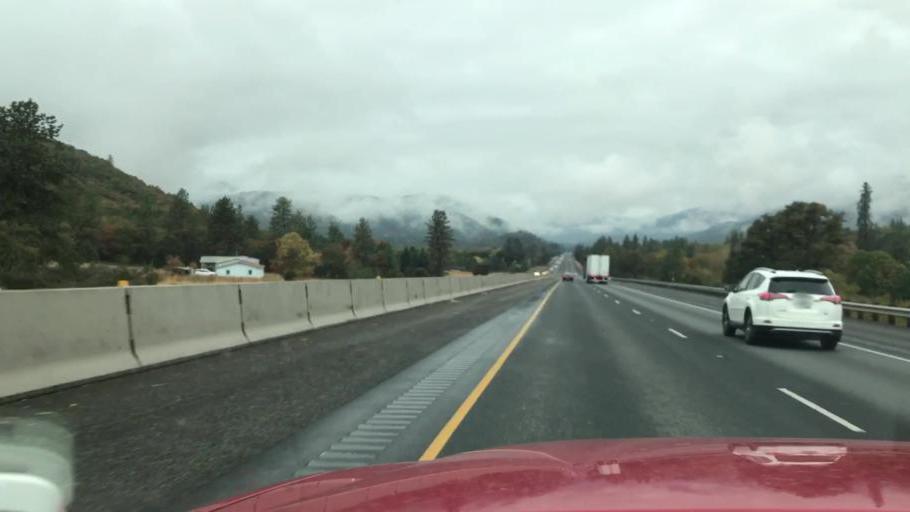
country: US
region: Oregon
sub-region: Jackson County
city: Gold Hill
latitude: 42.4152
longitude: -123.0007
